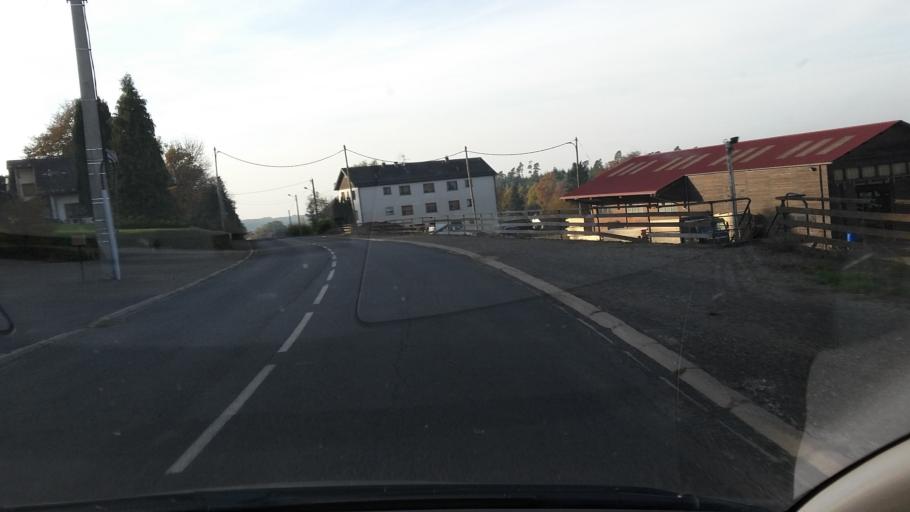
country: FR
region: Lorraine
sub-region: Departement de la Moselle
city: Dabo
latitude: 48.6852
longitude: 7.2185
